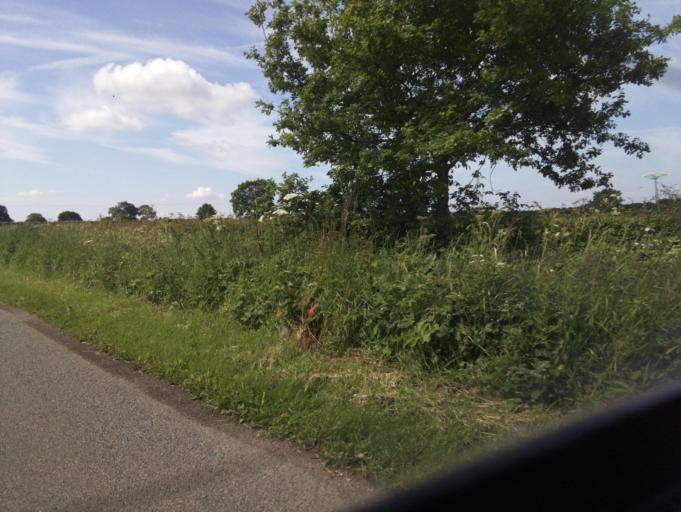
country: GB
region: England
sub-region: Lincolnshire
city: Skellingthorpe
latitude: 53.1413
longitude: -0.6332
